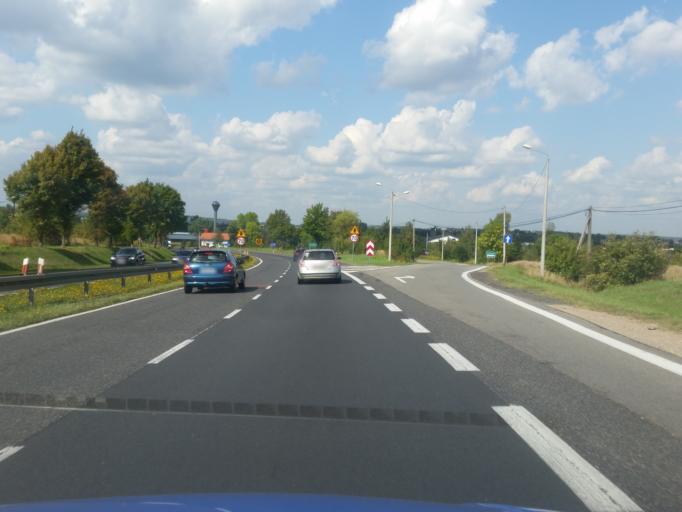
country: PL
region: Silesian Voivodeship
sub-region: Powiat myszkowski
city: Kozieglowy
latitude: 50.5881
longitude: 19.1620
